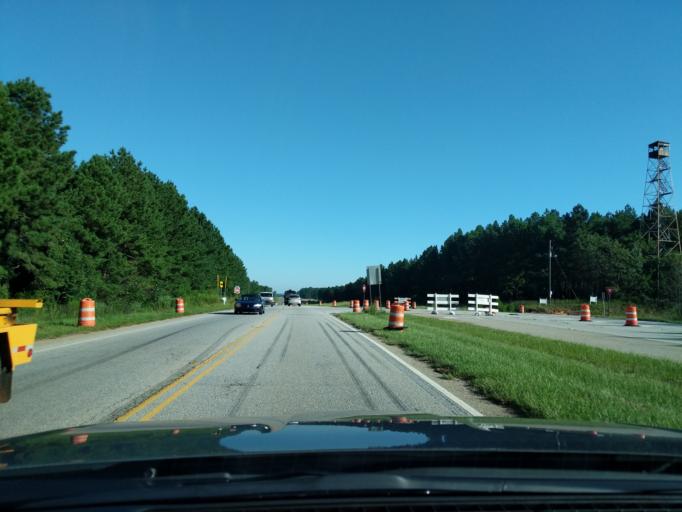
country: US
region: Georgia
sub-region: McDuffie County
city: Thomson
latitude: 33.5486
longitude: -82.5100
